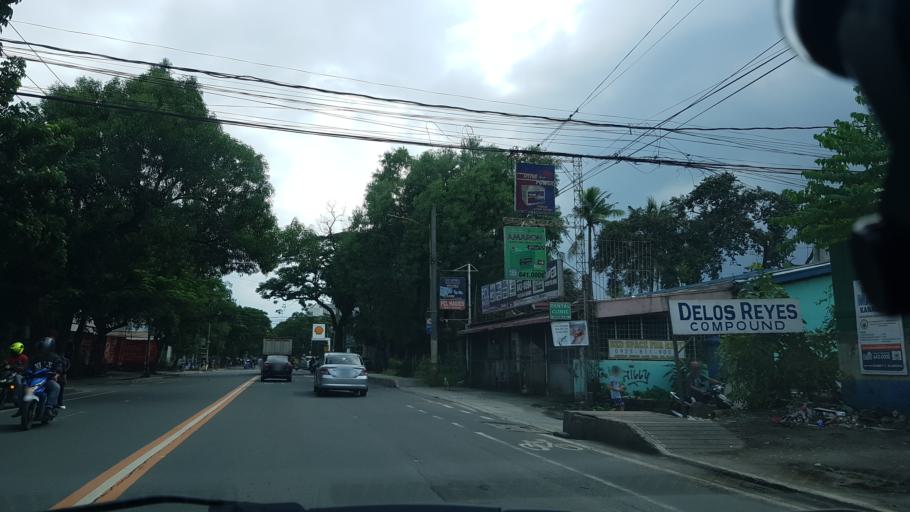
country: PH
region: Metro Manila
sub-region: Pasig
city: Pasig City
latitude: 14.5745
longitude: 121.0842
